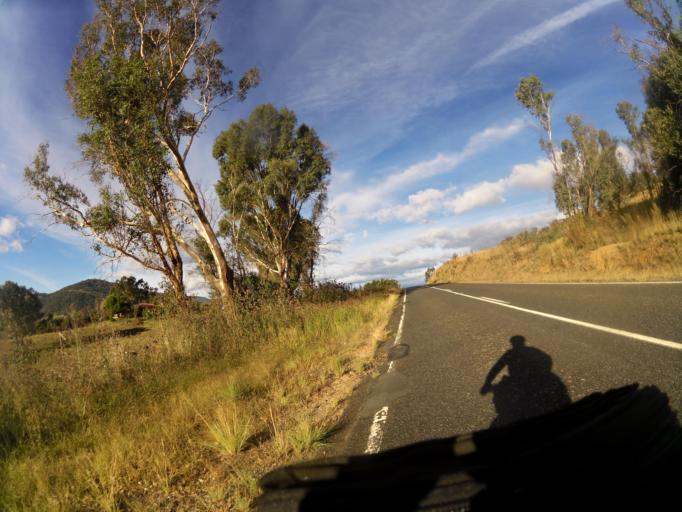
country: AU
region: New South Wales
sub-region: Greater Hume Shire
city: Holbrook
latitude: -36.0064
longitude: 147.8877
